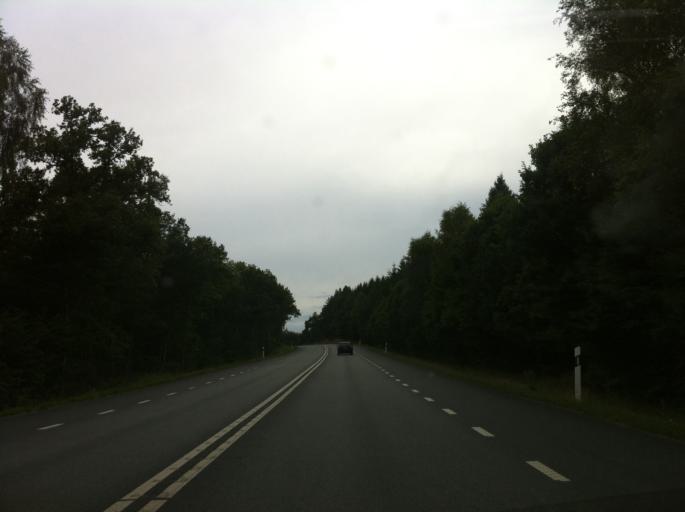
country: SE
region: Skane
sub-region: Hassleholms Kommun
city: Tormestorp
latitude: 56.0843
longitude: 13.7595
